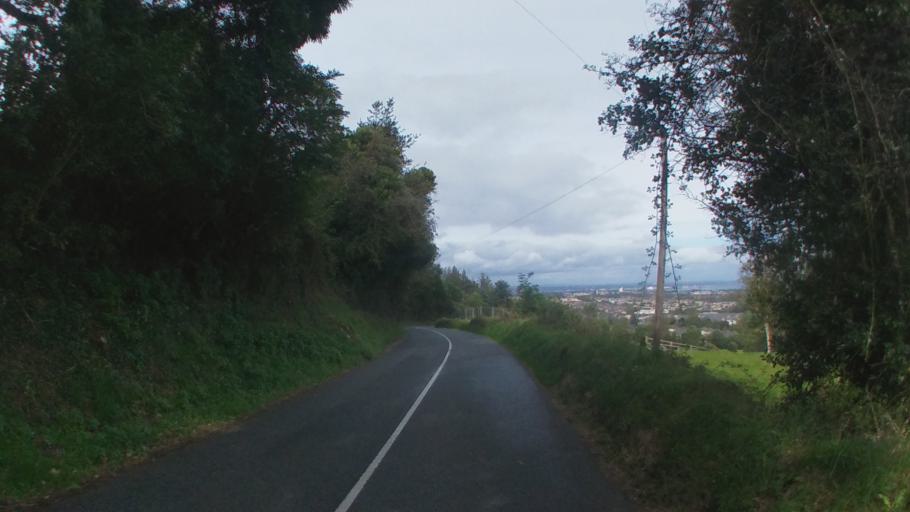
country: IE
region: Leinster
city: Sandyford
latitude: 53.2514
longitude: -6.2189
